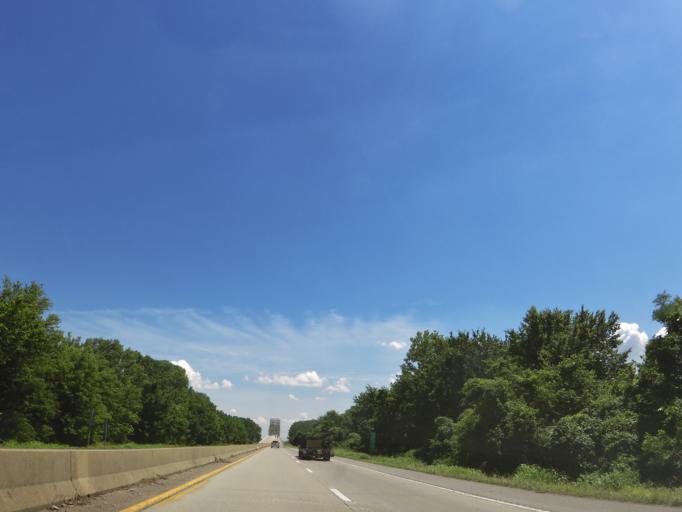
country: US
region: Missouri
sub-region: Pemiscot County
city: Caruthersville
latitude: 36.1250
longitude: -89.6189
